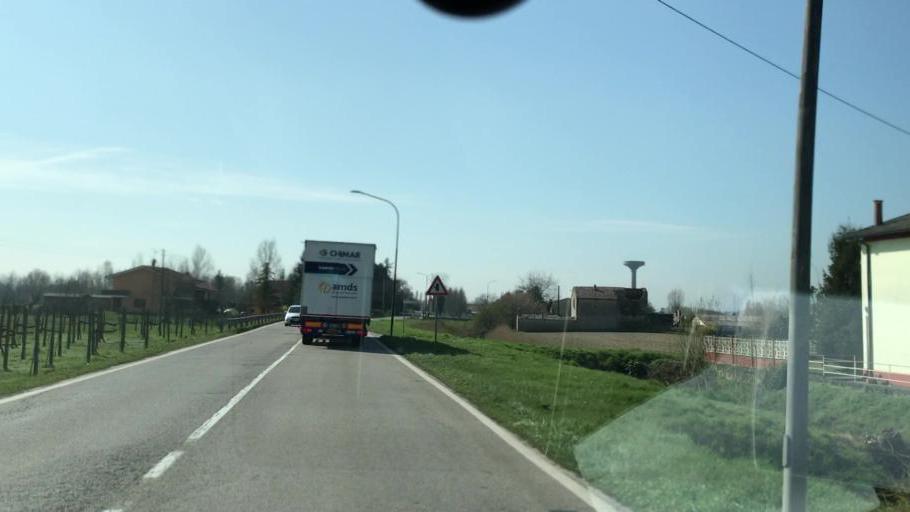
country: IT
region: Veneto
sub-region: Provincia di Rovigo
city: Castelnovo Bariano
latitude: 45.0301
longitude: 11.2985
